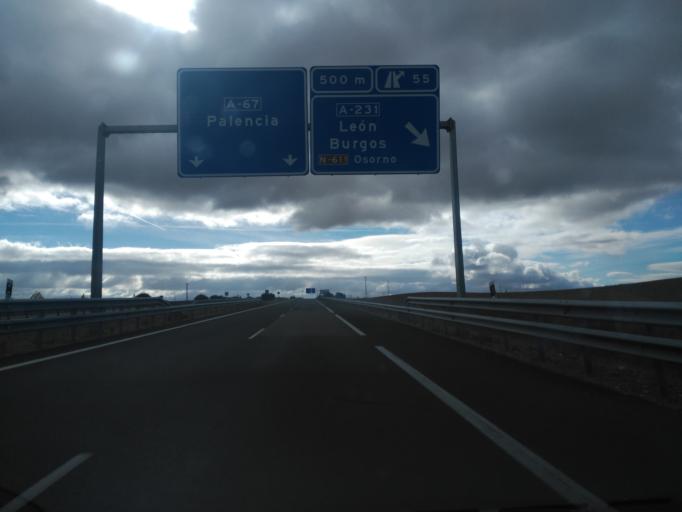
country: ES
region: Castille and Leon
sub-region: Provincia de Palencia
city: Abia de las Torres
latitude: 42.4179
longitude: -4.3888
